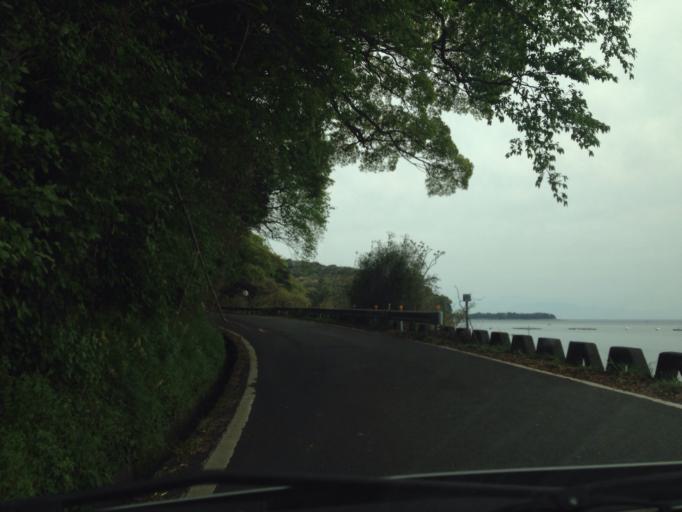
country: JP
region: Shizuoka
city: Heda
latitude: 35.0209
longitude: 138.8046
